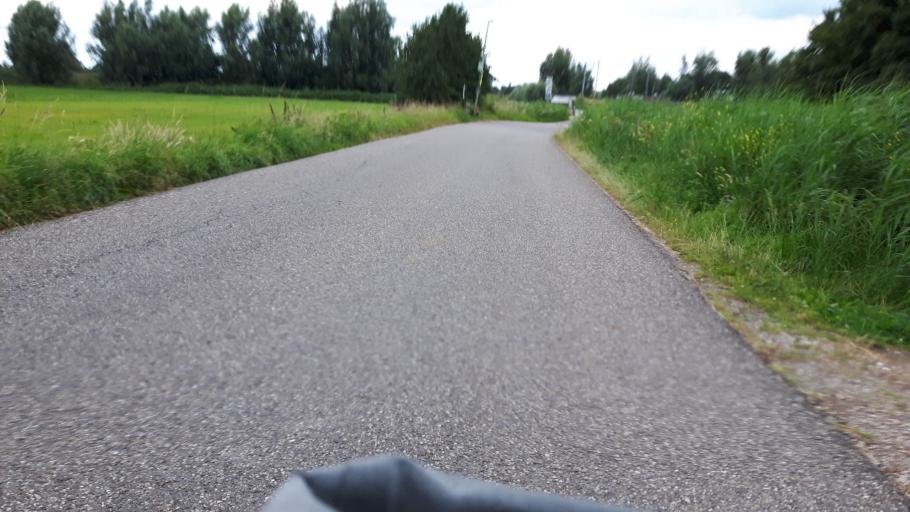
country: NL
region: South Holland
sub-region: Gemeente Vlist
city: Haastrecht
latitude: 52.0227
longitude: 4.8042
